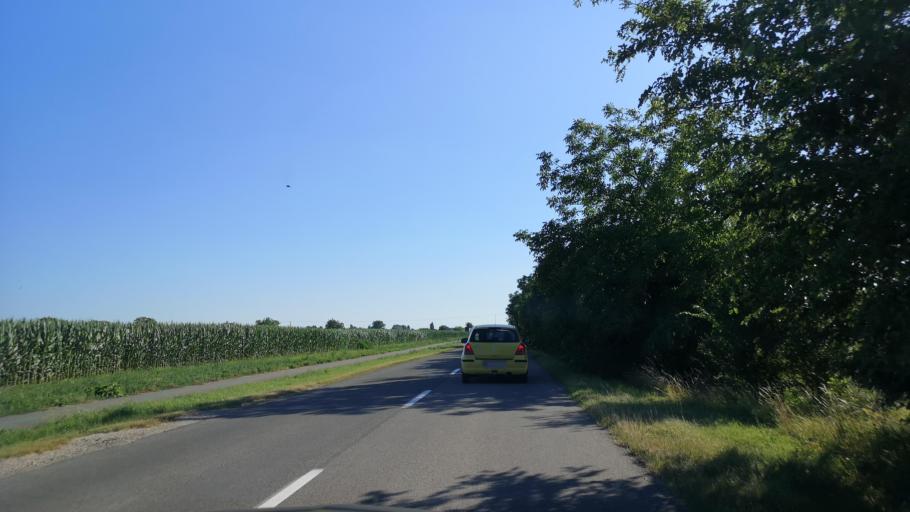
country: SK
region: Trnavsky
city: Dunajska Streda
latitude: 48.0340
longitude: 17.5477
